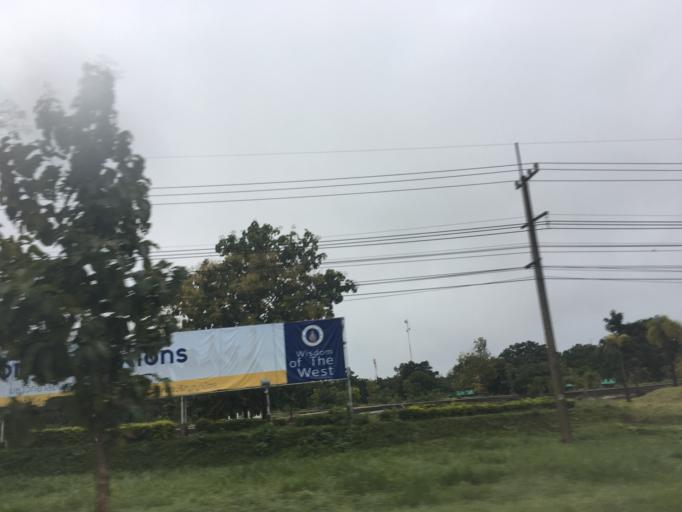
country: TH
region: Kanchanaburi
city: Sai Yok
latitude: 14.1307
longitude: 99.1623
